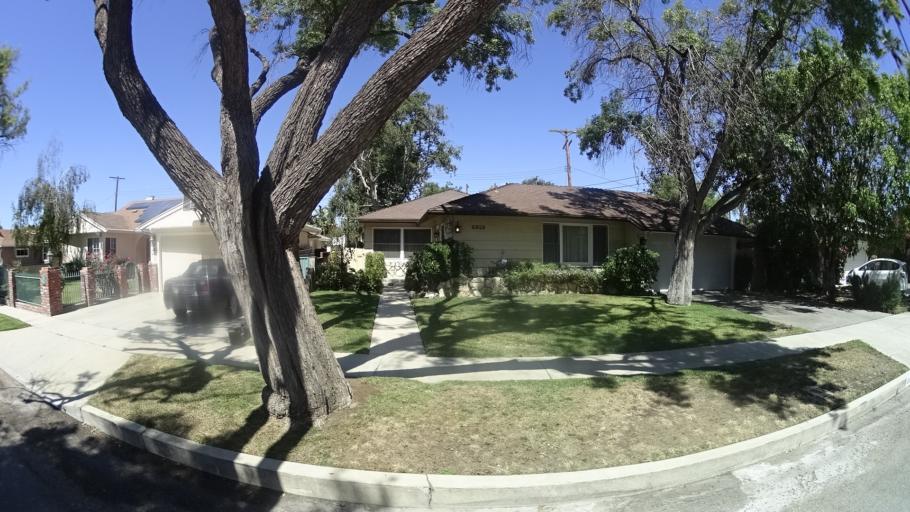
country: US
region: California
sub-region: Los Angeles County
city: Van Nuys
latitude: 34.1963
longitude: -118.4958
